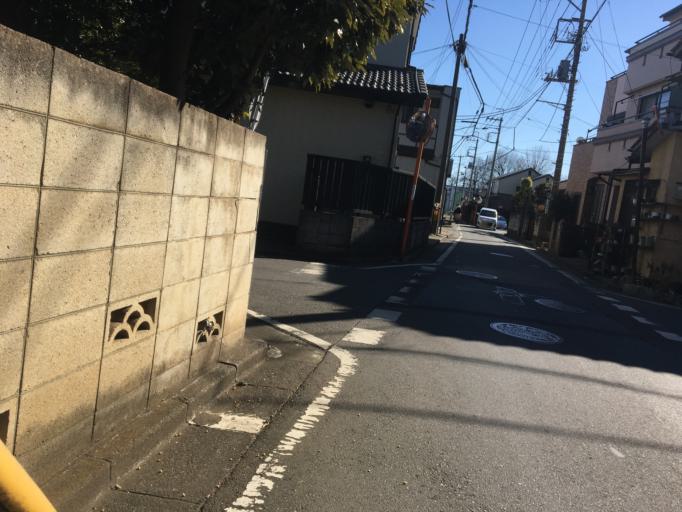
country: JP
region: Saitama
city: Oi
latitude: 35.8394
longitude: 139.5193
